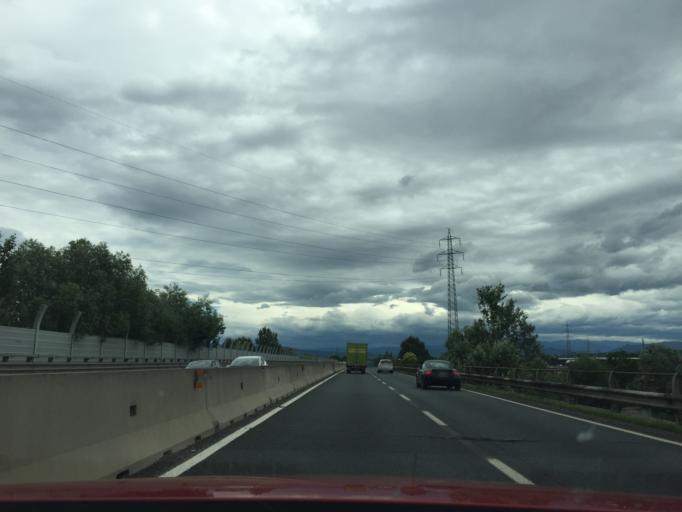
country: IT
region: Tuscany
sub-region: Province of Florence
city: Lastra a Signa
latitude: 43.7735
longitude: 11.1357
